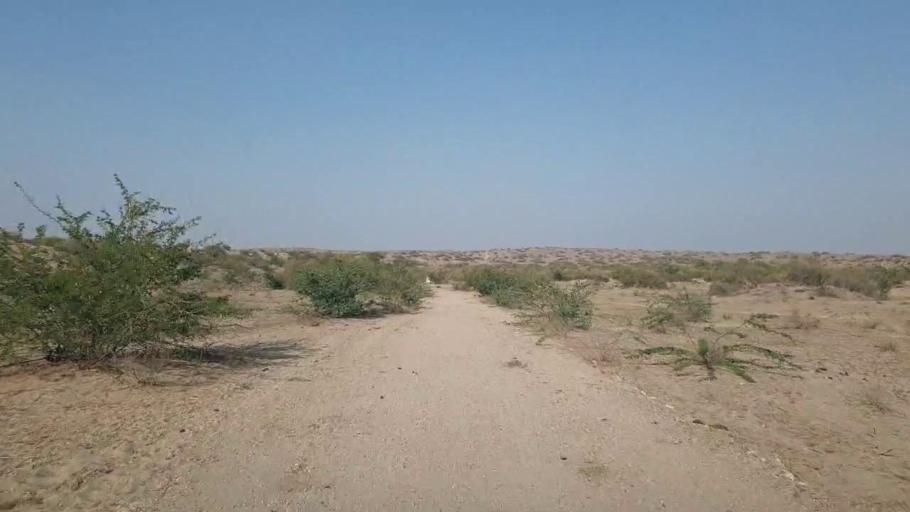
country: PK
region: Sindh
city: Dhoro Naro
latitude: 25.5083
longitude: 69.6042
